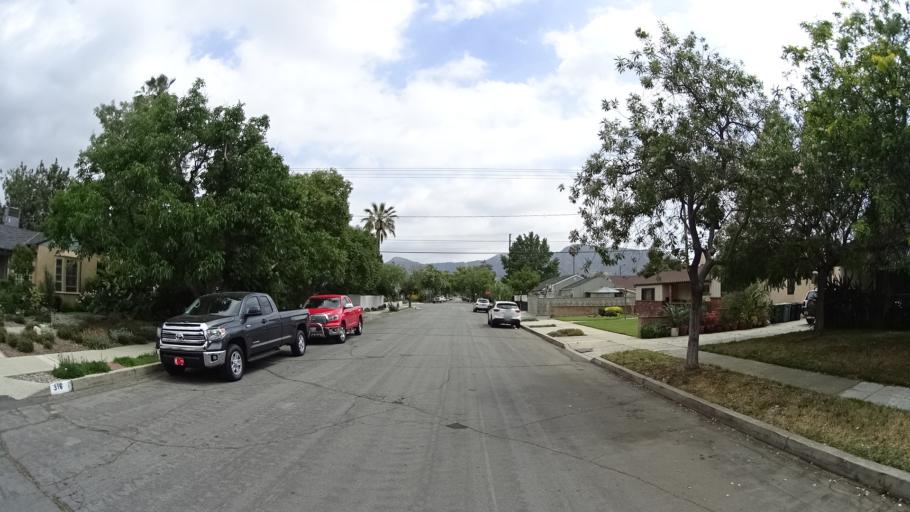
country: US
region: California
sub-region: Los Angeles County
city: Burbank
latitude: 34.1667
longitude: -118.3297
